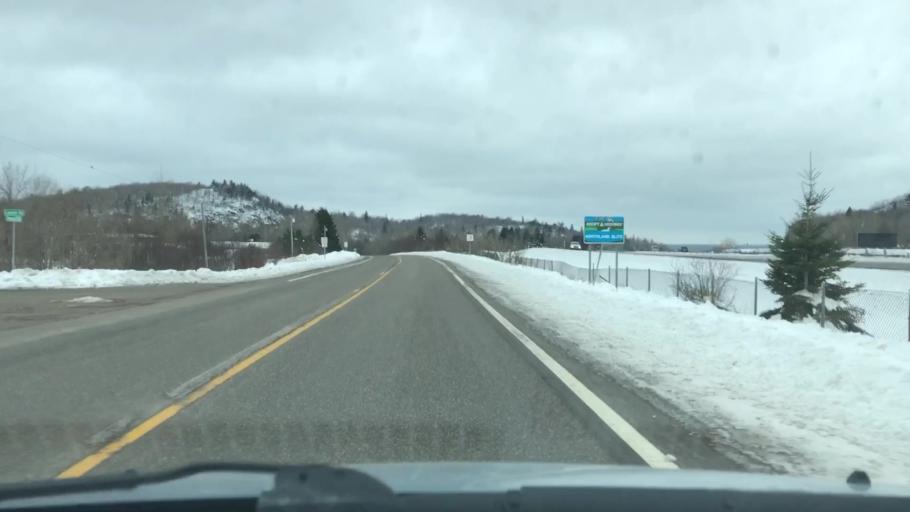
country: US
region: Minnesota
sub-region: Saint Louis County
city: Proctor
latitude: 46.7124
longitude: -92.2591
